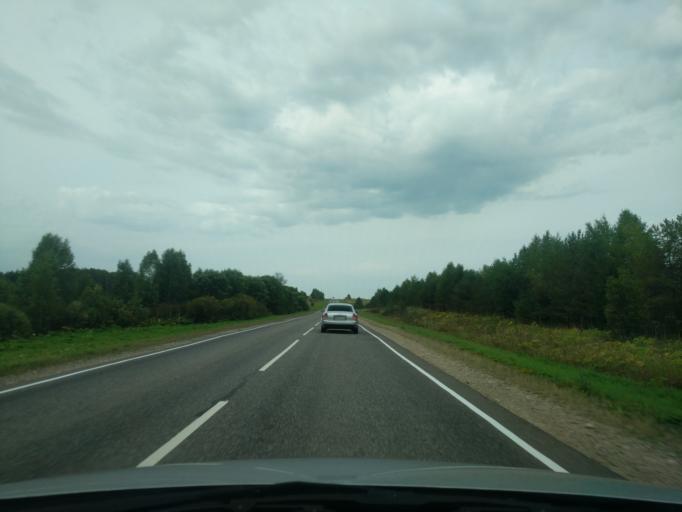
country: RU
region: Kirov
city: Mirnyy
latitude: 58.2728
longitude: 47.7836
